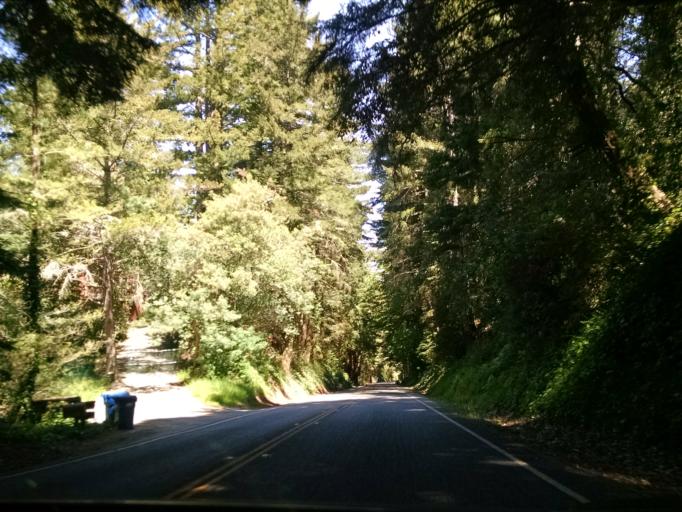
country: US
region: California
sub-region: San Mateo County
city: Portola Valley
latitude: 37.3799
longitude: -122.2629
